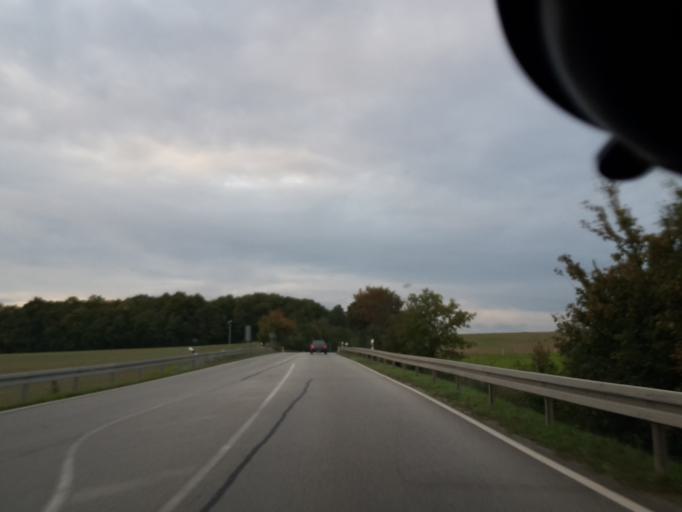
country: DE
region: Hesse
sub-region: Regierungsbezirk Darmstadt
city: Idstein
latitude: 50.2279
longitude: 8.1992
